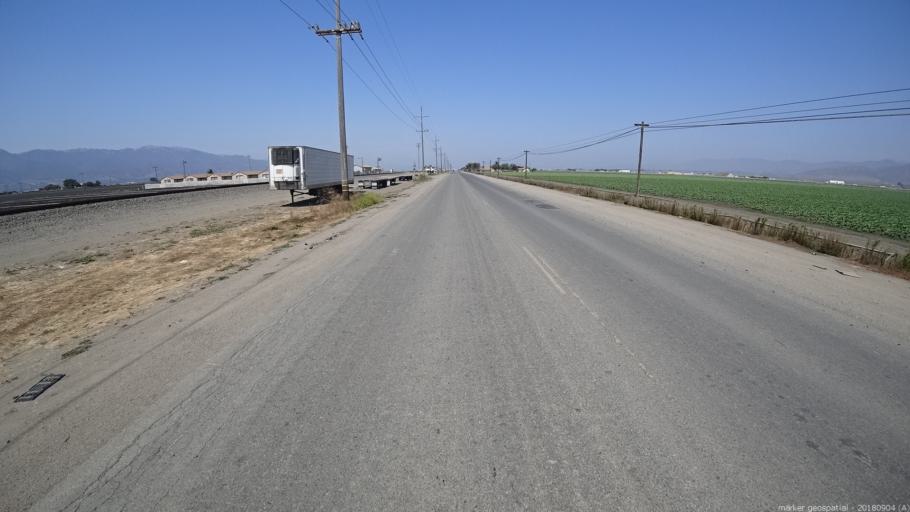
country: US
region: California
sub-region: Monterey County
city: Gonzales
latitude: 36.5175
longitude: -121.4585
